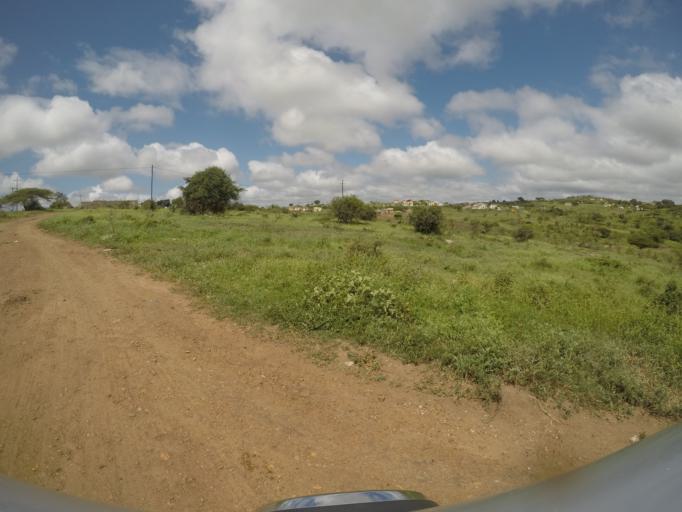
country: ZA
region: KwaZulu-Natal
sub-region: uThungulu District Municipality
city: Empangeni
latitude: -28.5732
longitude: 31.8391
